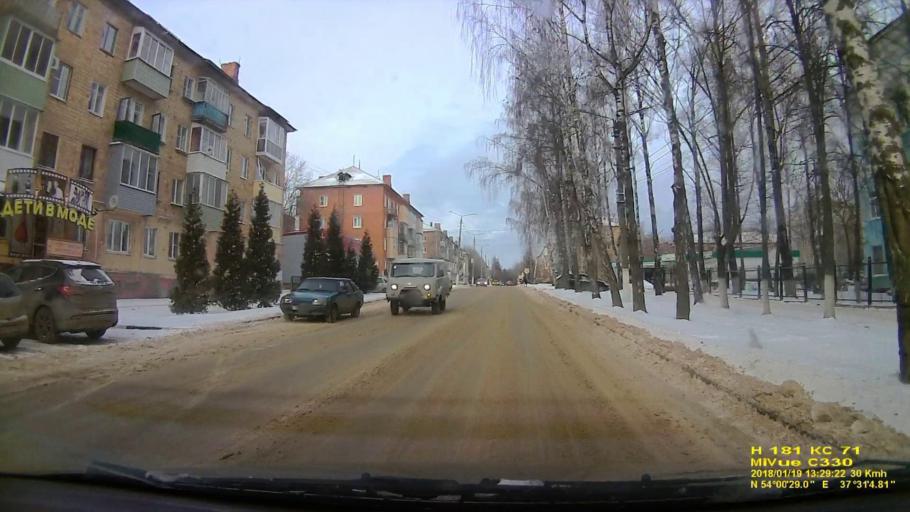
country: RU
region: Tula
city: Shchekino
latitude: 54.0081
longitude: 37.5180
